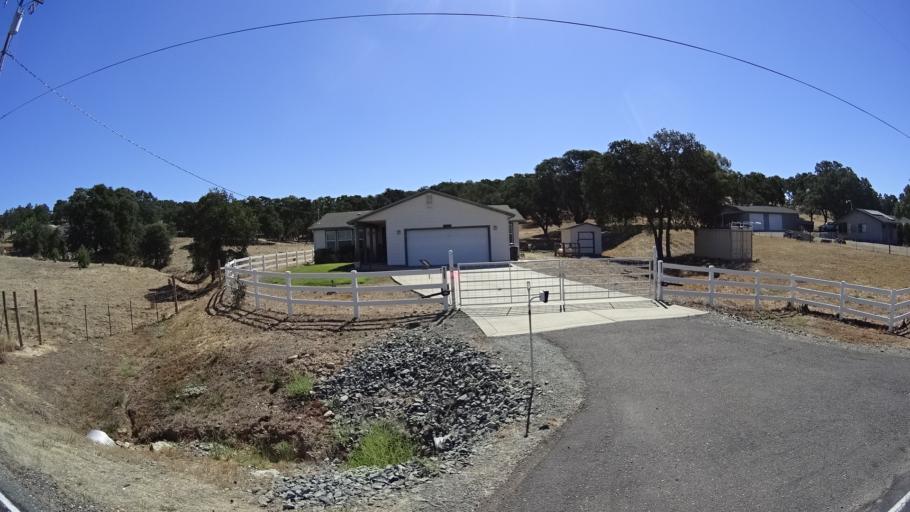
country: US
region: California
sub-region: Calaveras County
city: Rancho Calaveras
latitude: 38.1075
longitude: -120.8780
